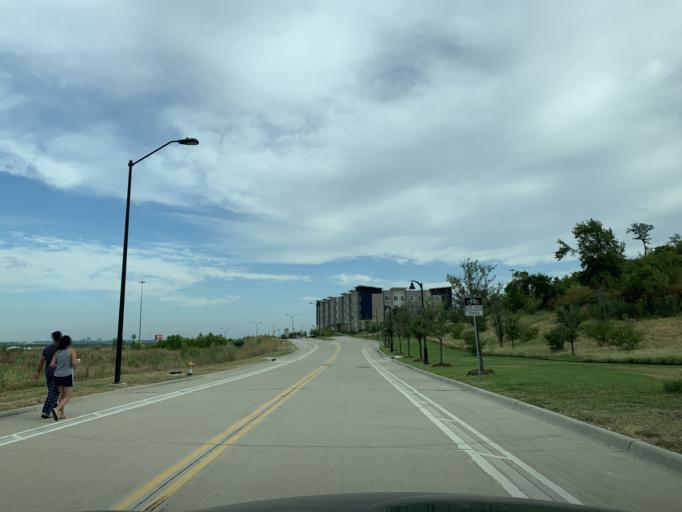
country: US
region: Texas
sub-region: Dallas County
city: Cockrell Hill
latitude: 32.7639
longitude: -96.8762
